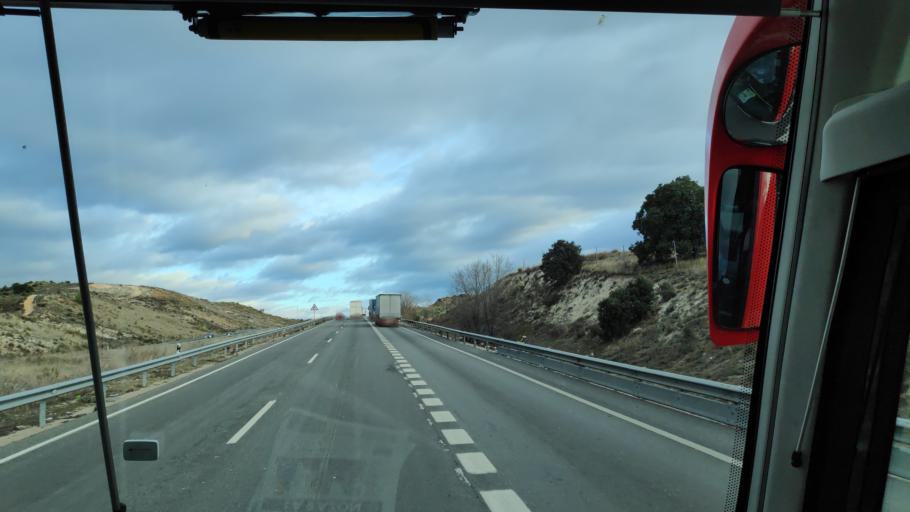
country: ES
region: Madrid
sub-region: Provincia de Madrid
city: Tielmes
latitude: 40.1988
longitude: -3.3126
